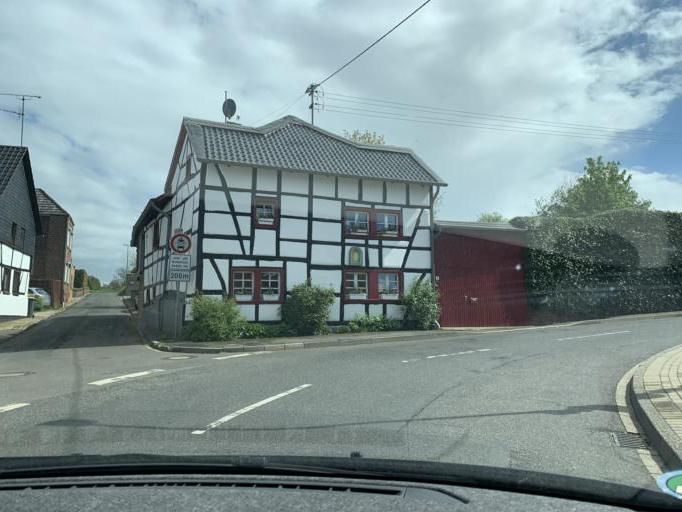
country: DE
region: North Rhine-Westphalia
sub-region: Regierungsbezirk Koln
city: Bad Munstereifel
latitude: 50.5926
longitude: 6.7154
